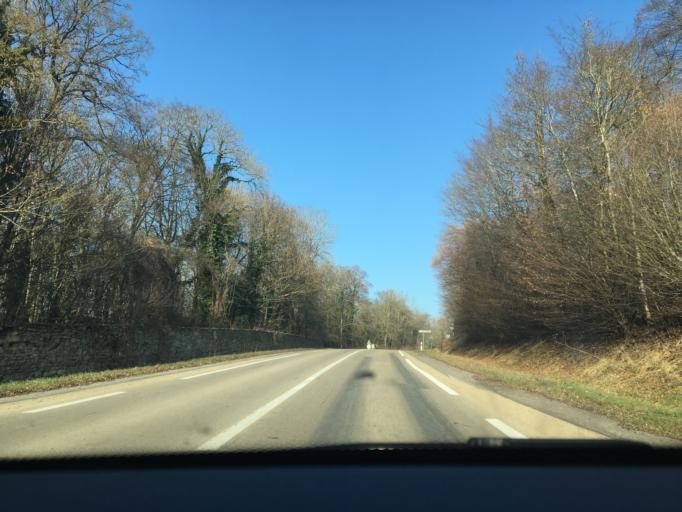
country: FR
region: Ile-de-France
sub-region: Departement des Yvelines
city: Follainville-Dennemont
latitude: 49.0298
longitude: 1.7469
